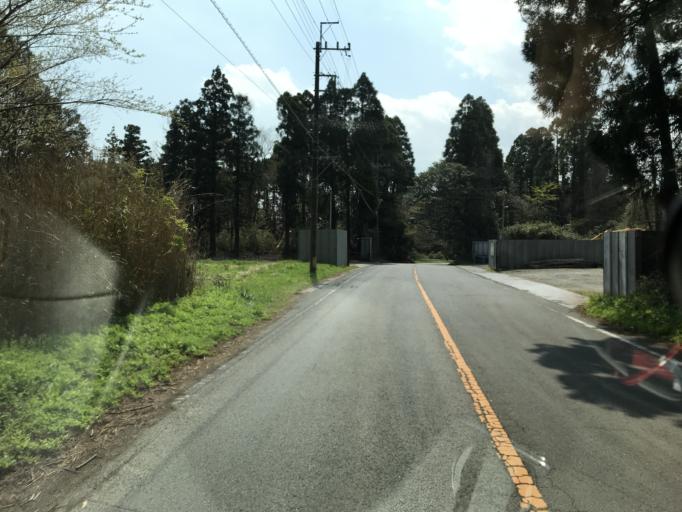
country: JP
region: Chiba
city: Omigawa
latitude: 35.8724
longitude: 140.5695
